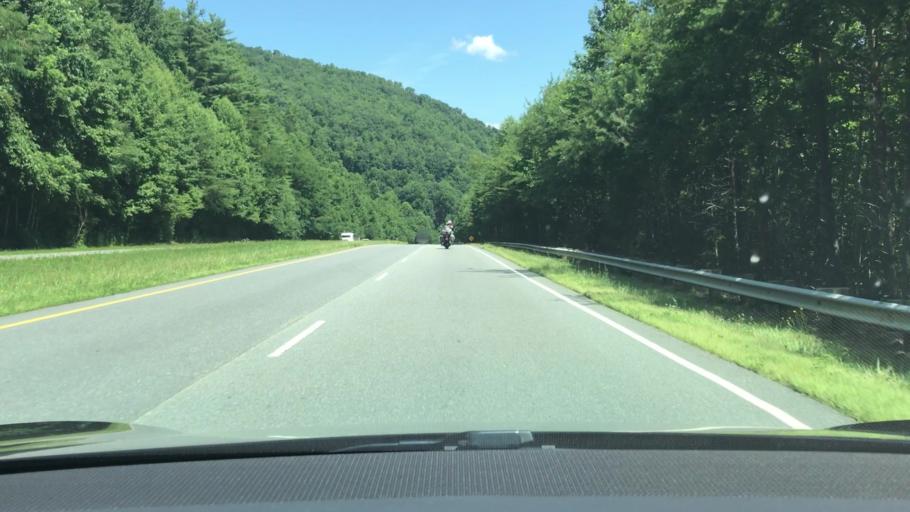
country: US
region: North Carolina
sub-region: Jackson County
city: Sylva
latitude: 35.3491
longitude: -83.2574
